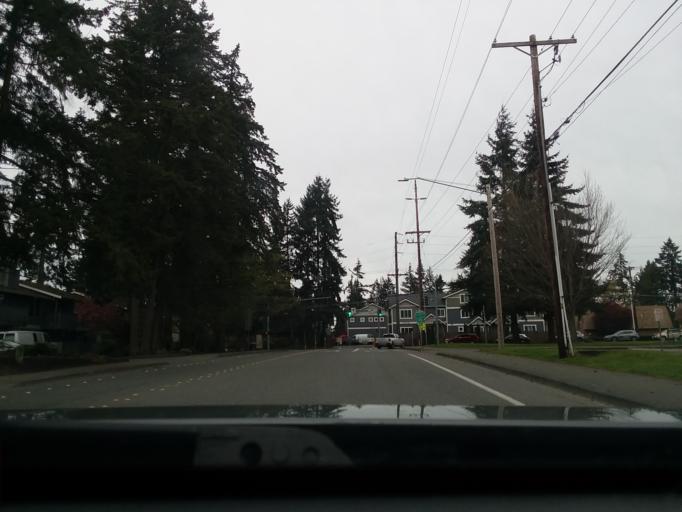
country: US
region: Washington
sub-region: Snohomish County
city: Lynnwood
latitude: 47.8106
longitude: -122.3347
